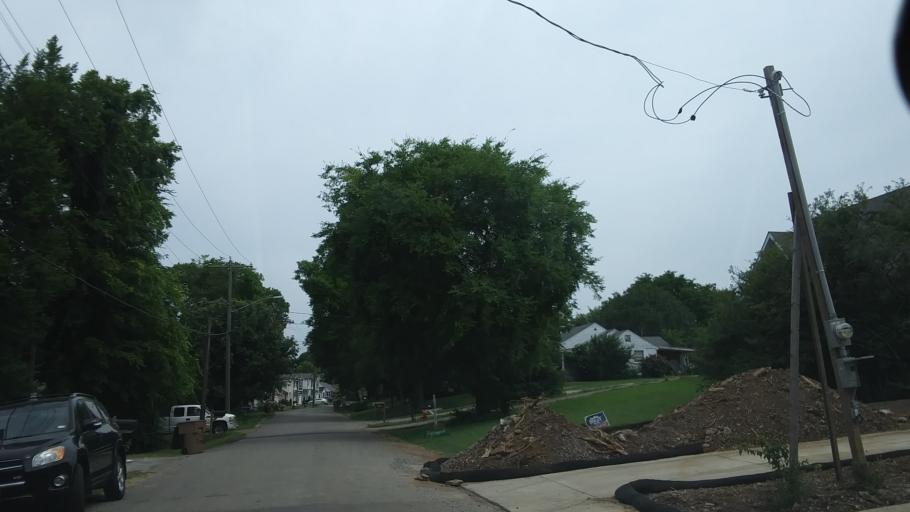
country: US
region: Tennessee
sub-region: Davidson County
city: Belle Meade
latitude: 36.1514
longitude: -86.8664
